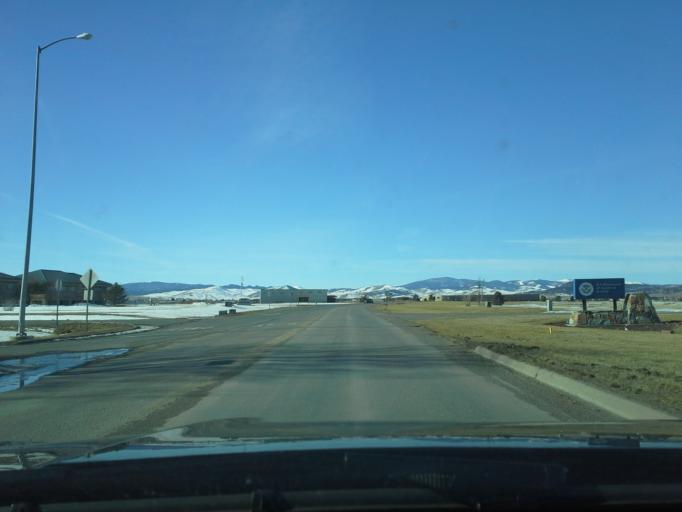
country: US
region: Montana
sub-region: Lewis and Clark County
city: Helena
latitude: 46.6119
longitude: -111.9911
